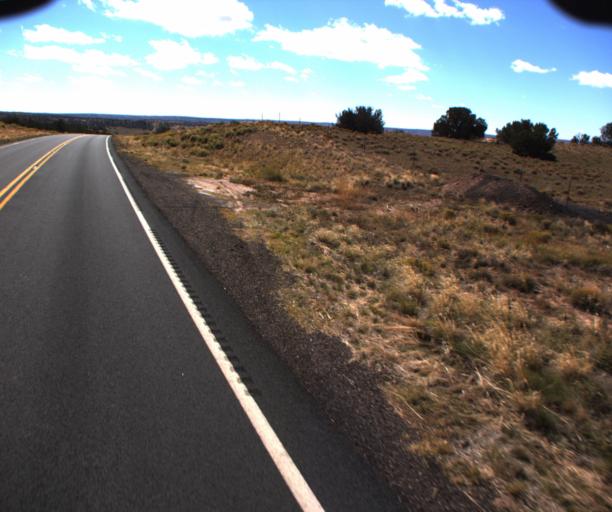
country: US
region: Arizona
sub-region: Apache County
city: Houck
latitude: 35.1084
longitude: -109.3172
